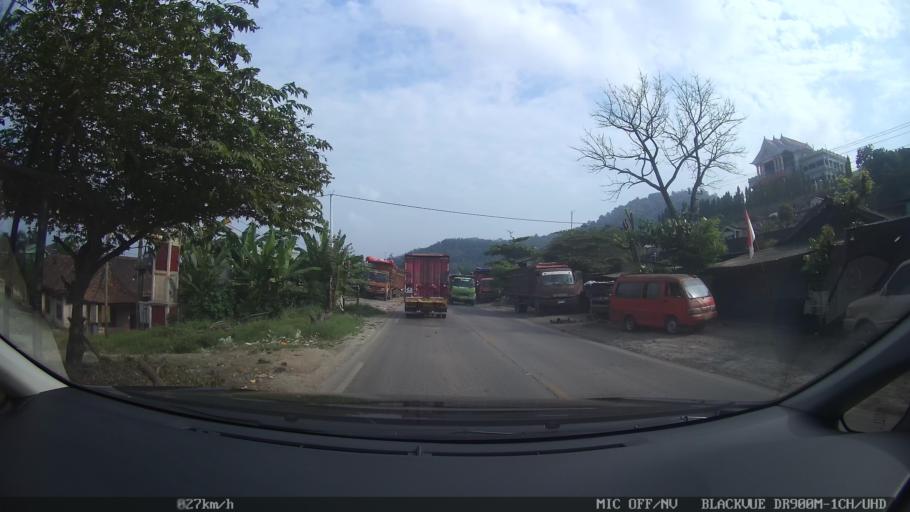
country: ID
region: Lampung
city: Panjang
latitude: -5.4661
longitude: 105.3224
